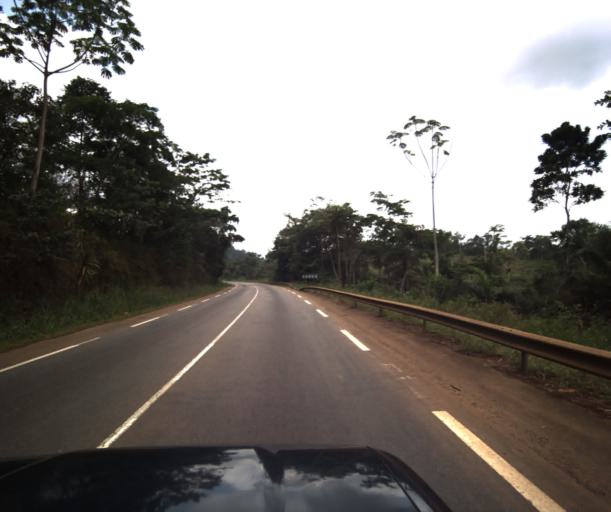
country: CM
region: Centre
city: Mbankomo
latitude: 3.7800
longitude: 11.0747
